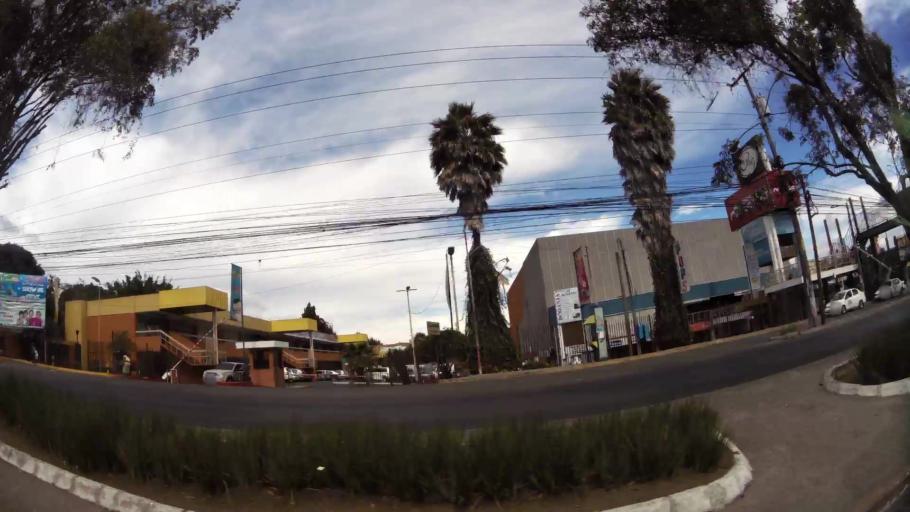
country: GT
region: Guatemala
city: Mixco
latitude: 14.6413
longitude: -90.5689
